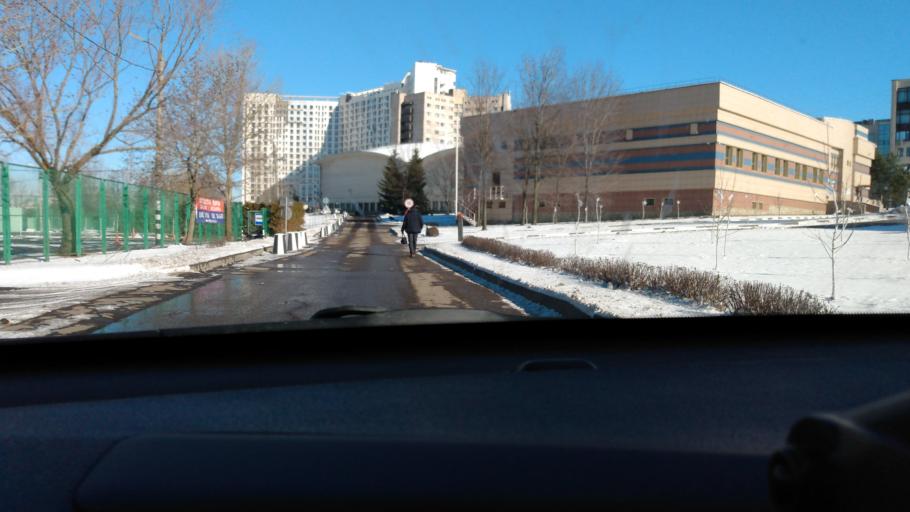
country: RU
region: Moscow
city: Nikol'skoye
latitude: 55.6714
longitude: 37.4844
